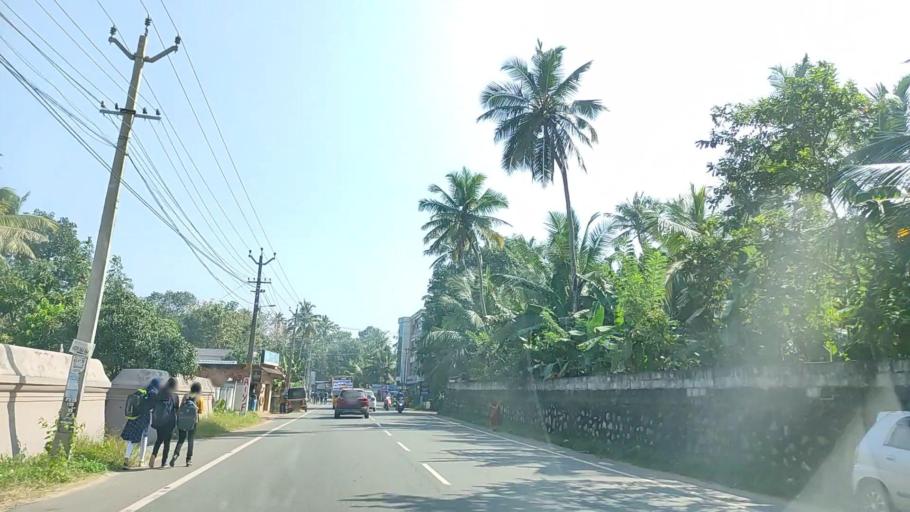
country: IN
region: Kerala
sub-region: Kollam
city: Punalur
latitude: 8.9344
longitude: 76.9427
